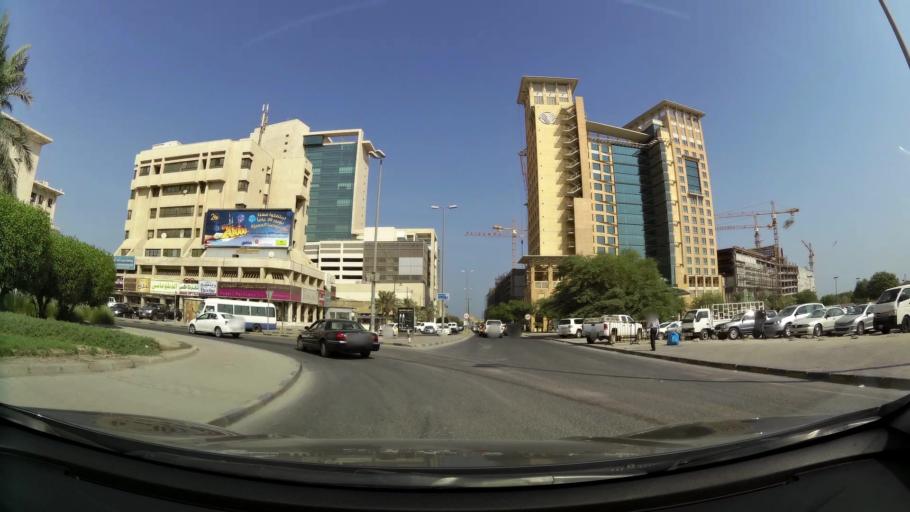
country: KW
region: Al Ahmadi
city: Al Fahahil
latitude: 29.0779
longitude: 48.1363
